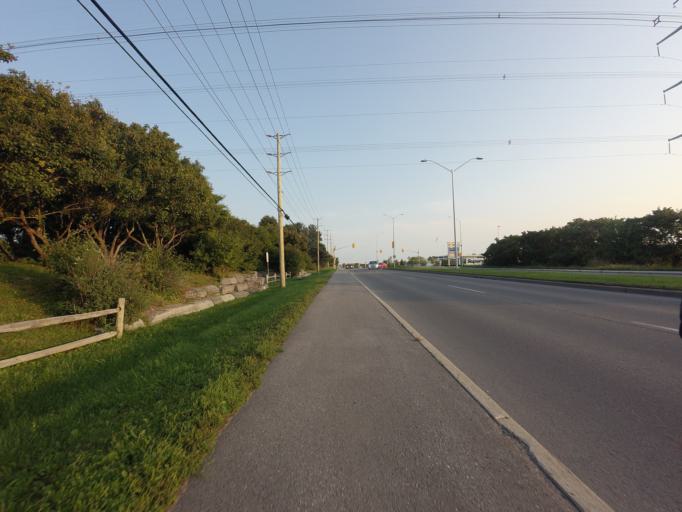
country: CA
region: Ontario
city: Bells Corners
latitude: 45.2852
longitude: -75.8663
